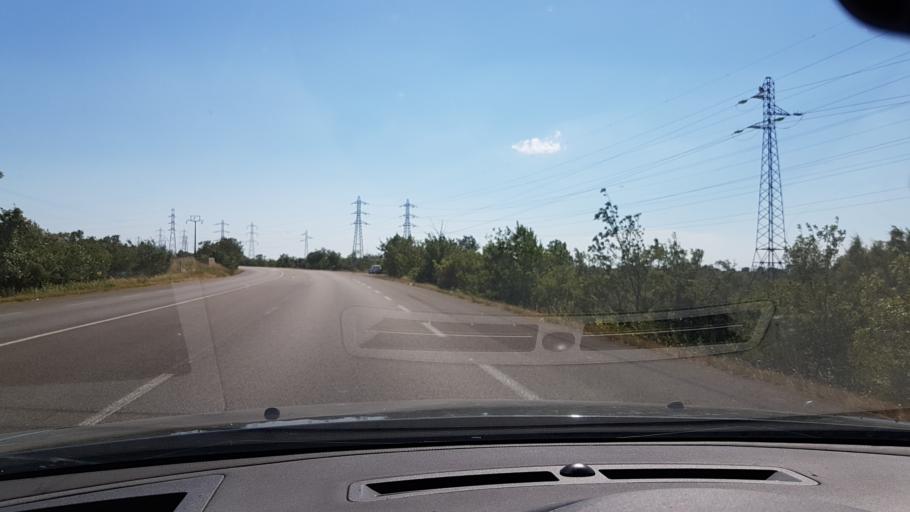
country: FR
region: Provence-Alpes-Cote d'Azur
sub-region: Departement des Bouches-du-Rhone
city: Port-Saint-Louis-du-Rhone
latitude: 43.4722
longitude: 4.8442
